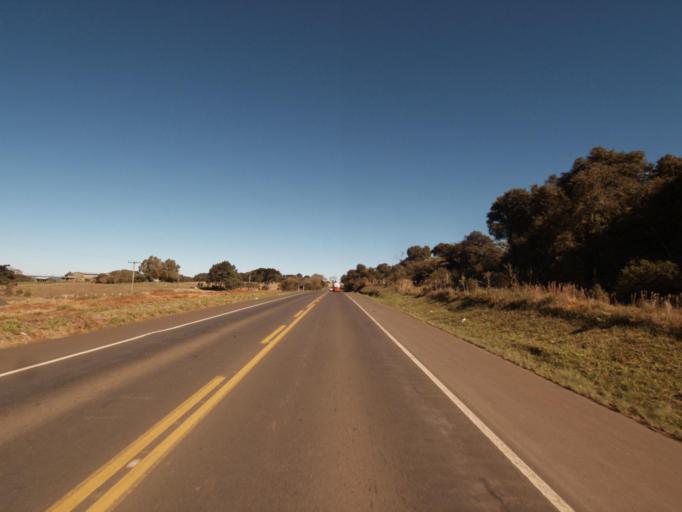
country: BR
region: Santa Catarina
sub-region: Xanxere
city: Xanxere
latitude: -26.8666
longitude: -52.2726
